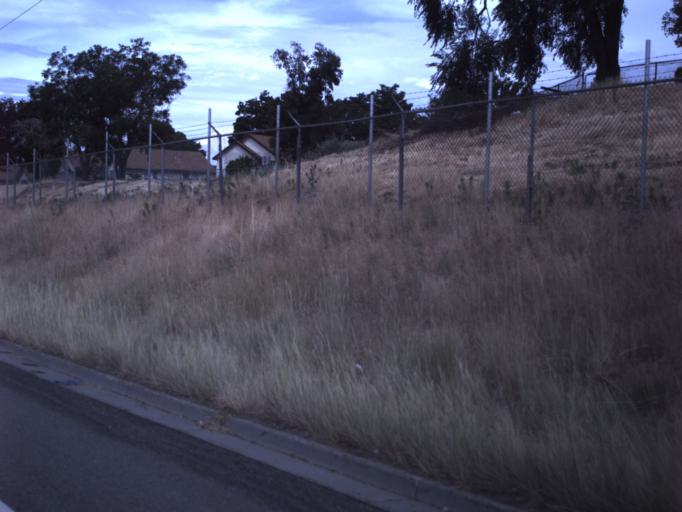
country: US
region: Utah
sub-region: Davis County
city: Hill Air Force Bace
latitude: 41.1036
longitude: -111.9911
